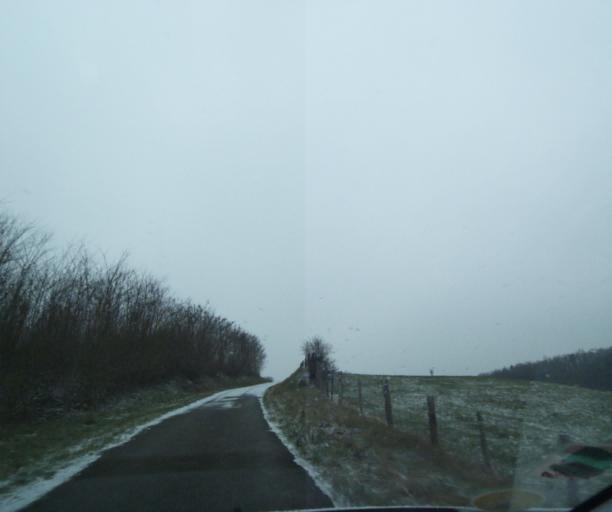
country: FR
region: Champagne-Ardenne
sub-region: Departement de la Haute-Marne
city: Wassy
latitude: 48.4655
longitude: 5.0087
